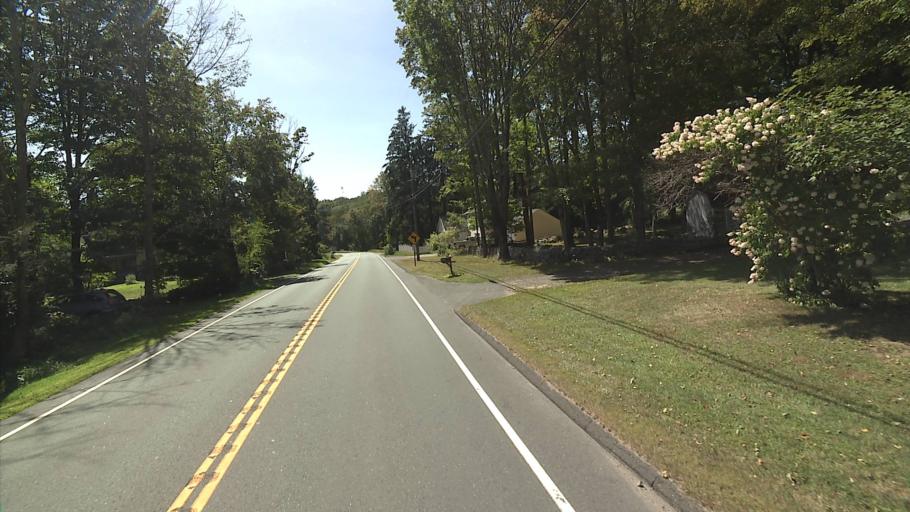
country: US
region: Connecticut
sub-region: New Haven County
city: Oxford
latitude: 41.4604
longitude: -73.1636
